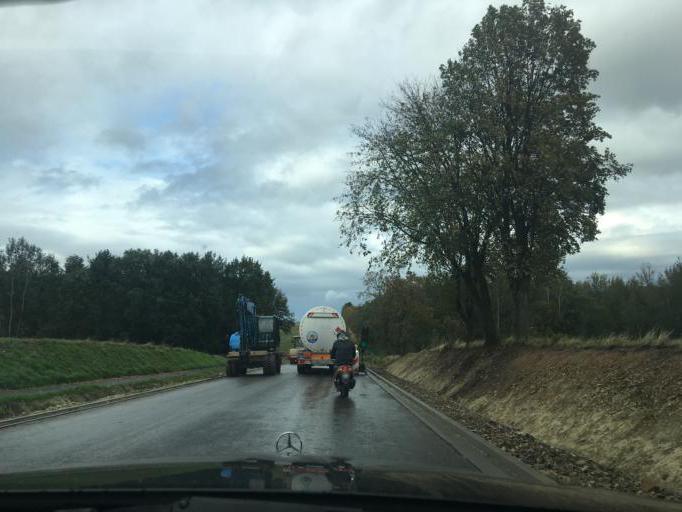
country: PL
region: Lublin Voivodeship
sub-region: Powiat lubelski
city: Wysokie
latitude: 50.9386
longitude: 22.6738
